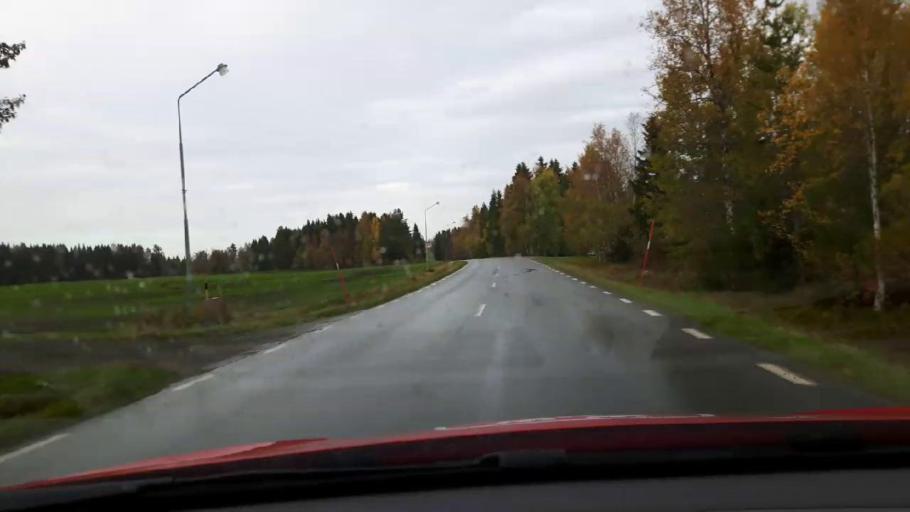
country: SE
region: Jaemtland
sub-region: Bergs Kommun
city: Hoverberg
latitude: 63.0243
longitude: 14.3440
